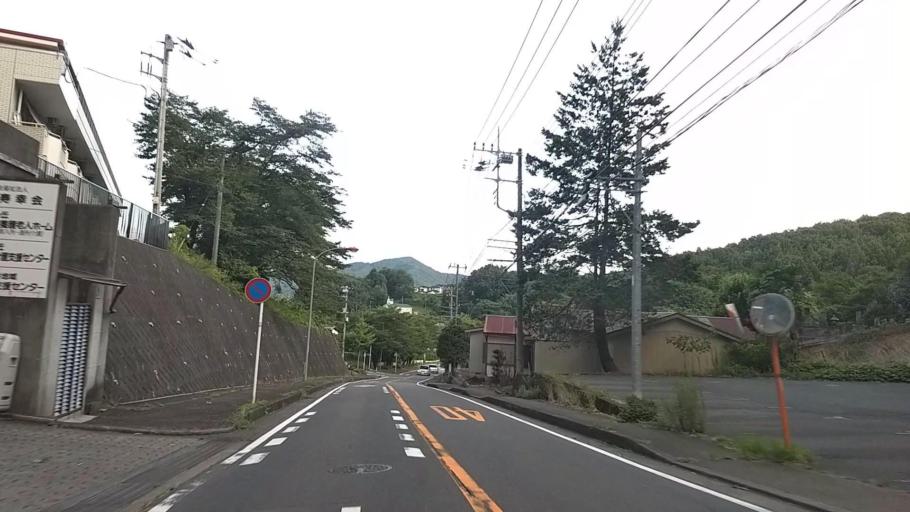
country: JP
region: Tokyo
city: Hachioji
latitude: 35.5804
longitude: 139.2620
